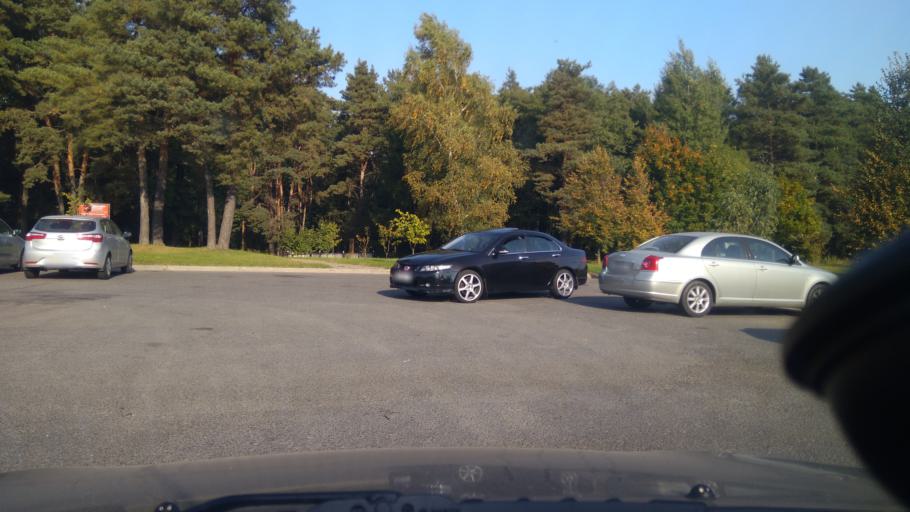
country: BY
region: Minsk
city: Vyaliki Trastsyanets
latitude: 53.8283
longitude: 27.7021
